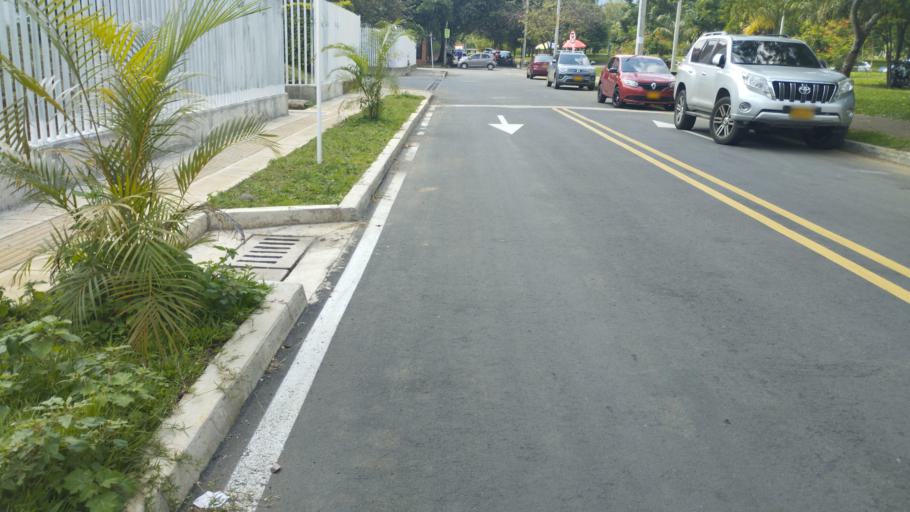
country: CO
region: Valle del Cauca
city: Cali
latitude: 3.3940
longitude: -76.5256
